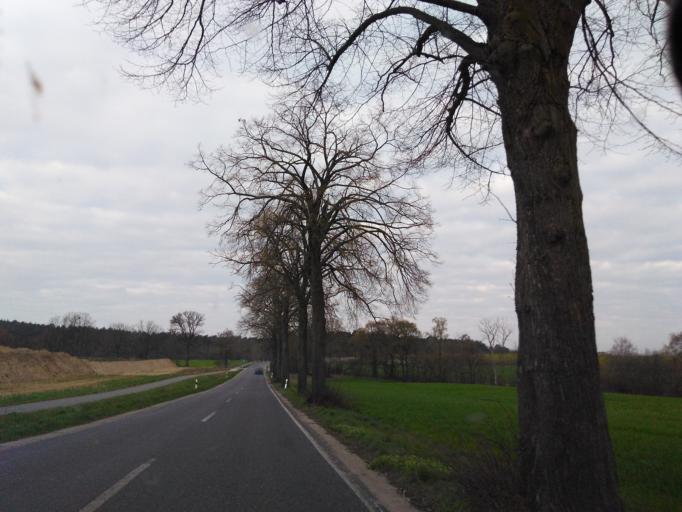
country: DE
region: Brandenburg
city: Strausberg
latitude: 52.5674
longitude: 13.9412
